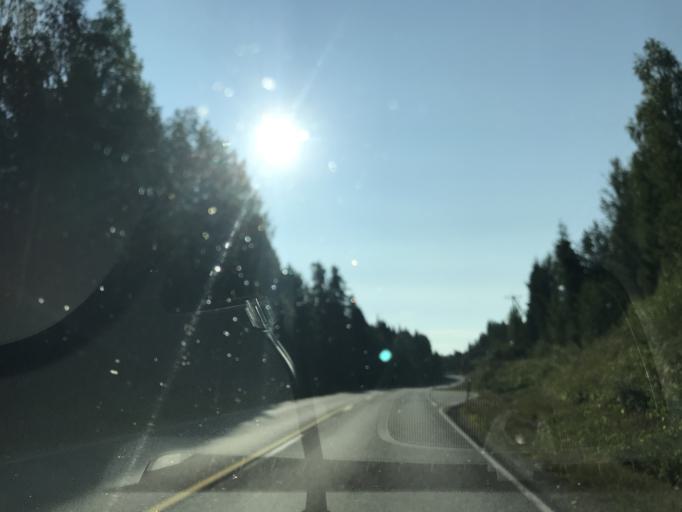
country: FI
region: Uusimaa
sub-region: Porvoo
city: Pukkila
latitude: 60.7695
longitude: 25.4985
